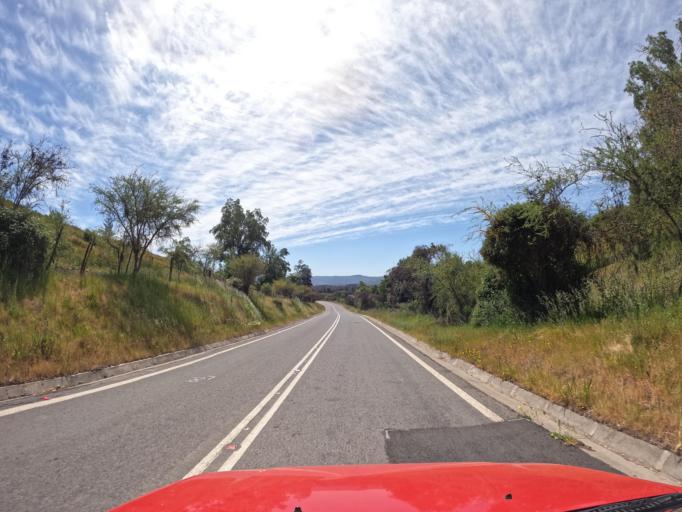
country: CL
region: Maule
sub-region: Provincia de Talca
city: Talca
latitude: -35.0636
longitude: -71.7352
